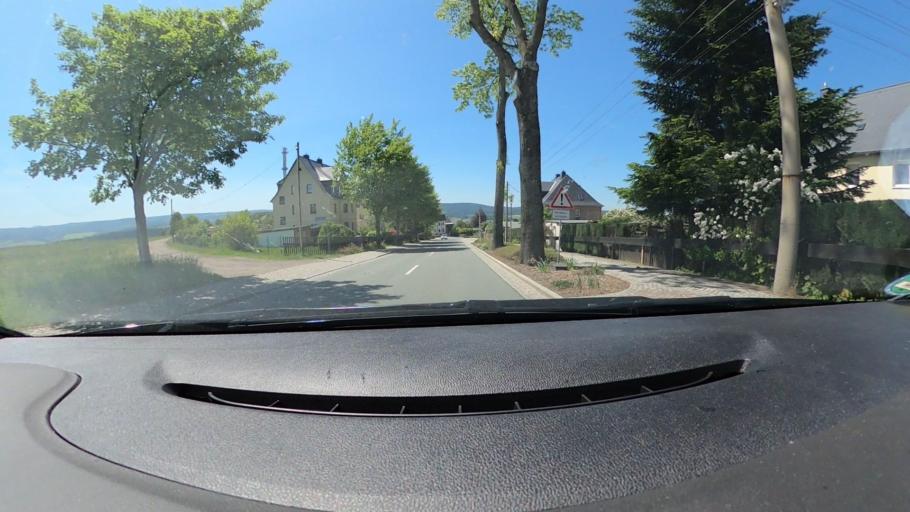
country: DE
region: Saxony
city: Beierfeld
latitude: 50.5674
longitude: 12.7988
